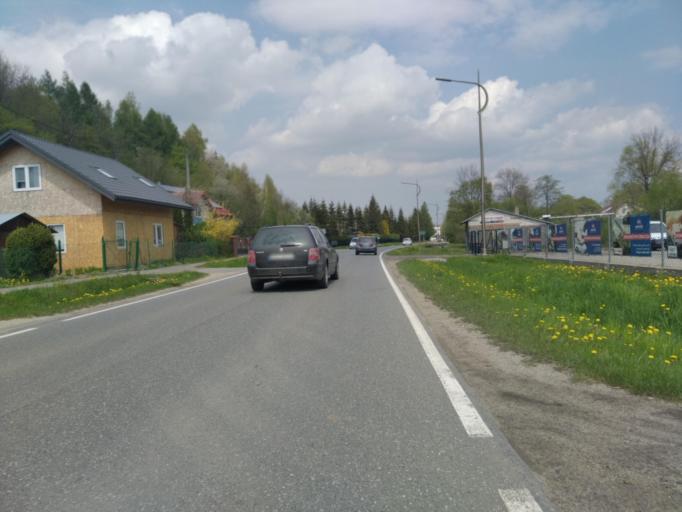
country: PL
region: Subcarpathian Voivodeship
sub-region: Powiat krosnienski
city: Rymanow
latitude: 49.5696
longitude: 21.8658
